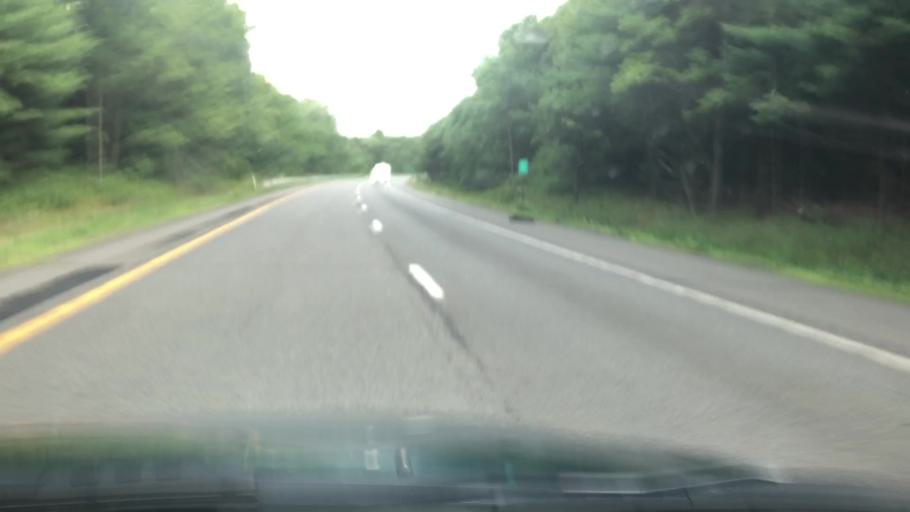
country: US
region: Pennsylvania
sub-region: Pike County
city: Milford
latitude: 41.3397
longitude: -74.8734
